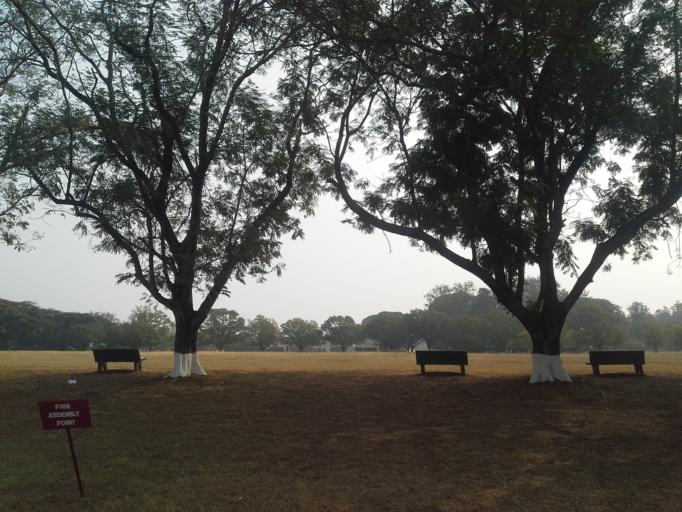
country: IN
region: Telangana
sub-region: Medak
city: Patancheru
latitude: 17.5114
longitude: 78.2755
